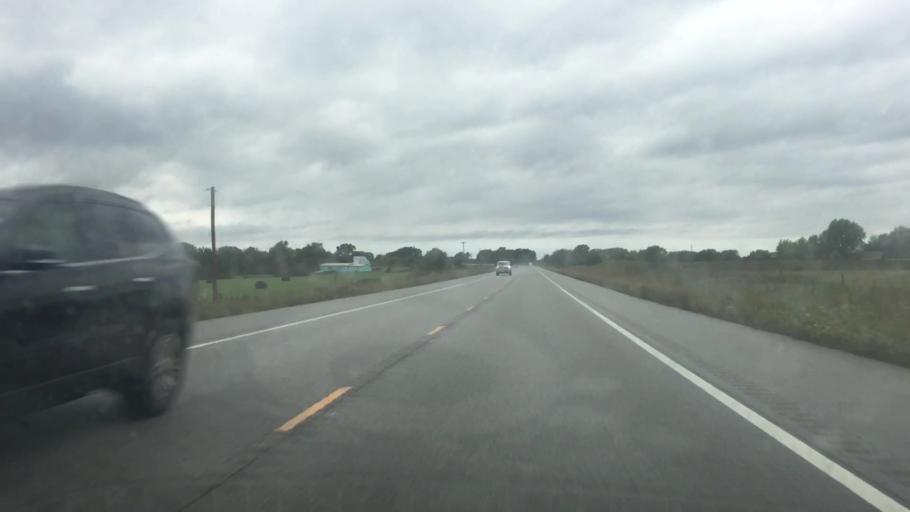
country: US
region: Kansas
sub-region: Miami County
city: Osawatomie
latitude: 38.4442
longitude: -94.9881
